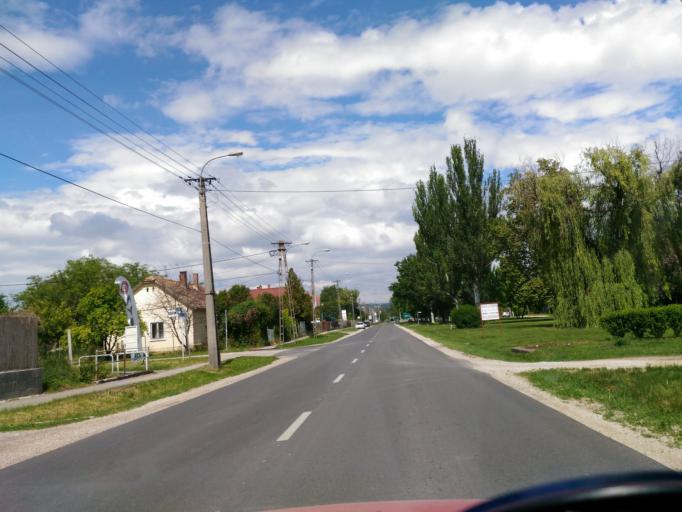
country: HU
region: Fejer
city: Kapolnasnyek
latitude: 47.2243
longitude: 18.6689
